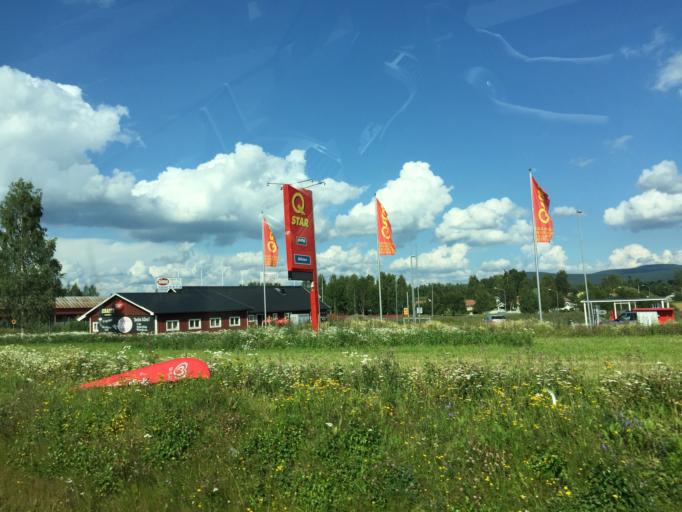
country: SE
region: Gaevleborg
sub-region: Bollnas Kommun
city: Arbra
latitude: 61.4622
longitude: 16.3700
